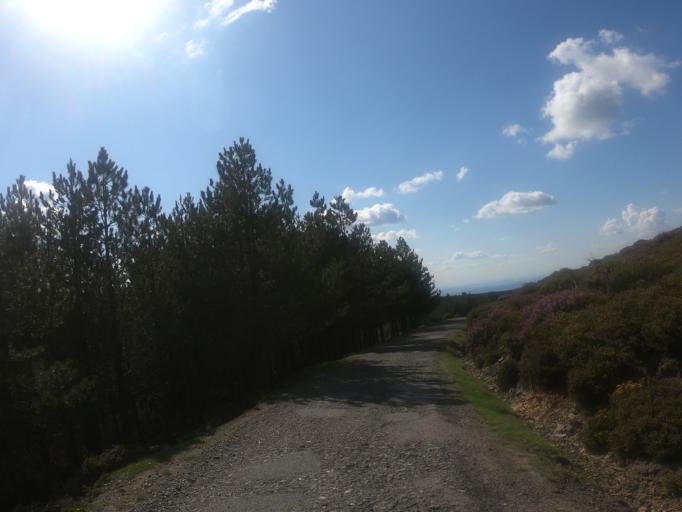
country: PT
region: Vila Real
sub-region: Mesao Frio
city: Mesao Frio
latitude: 41.2471
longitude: -7.8901
